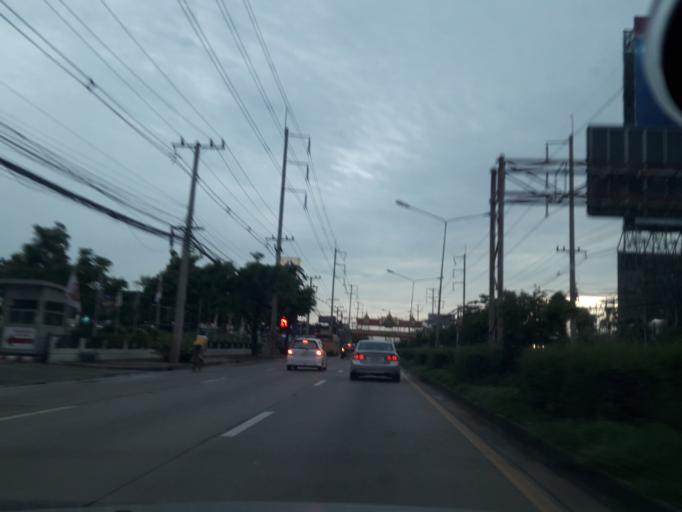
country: TH
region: Pathum Thani
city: Lam Luk Ka
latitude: 13.9346
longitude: 100.7419
